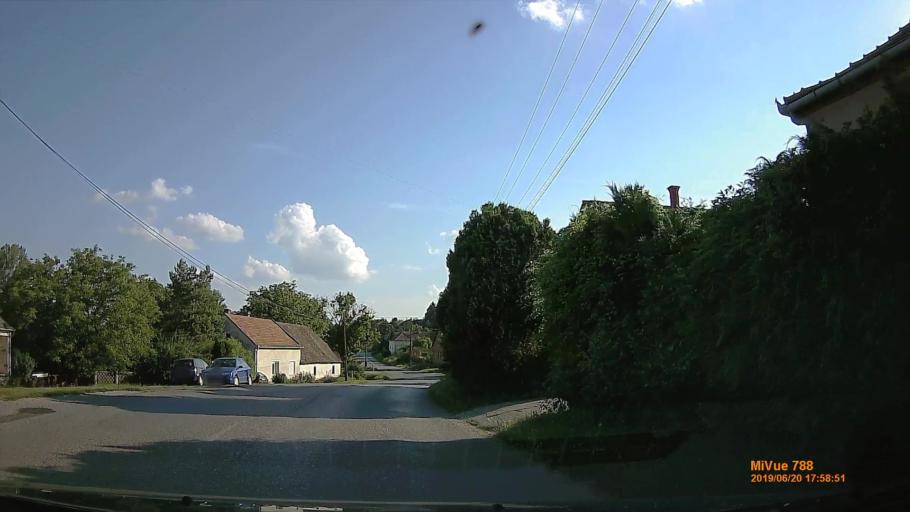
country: HU
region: Baranya
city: Buekkoesd
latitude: 46.1016
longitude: 17.9886
